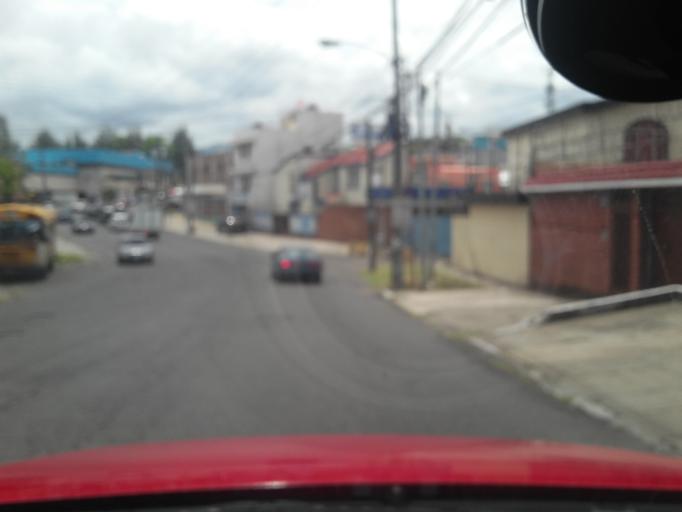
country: GT
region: Guatemala
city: Mixco
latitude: 14.6427
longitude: -90.5662
